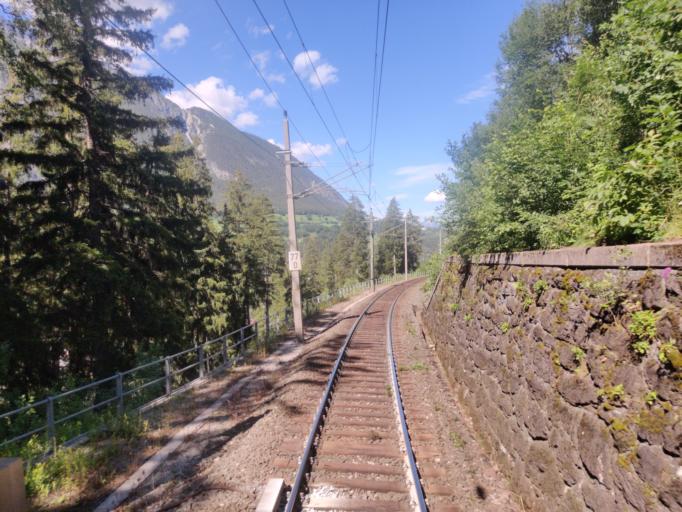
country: AT
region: Tyrol
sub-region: Politischer Bezirk Landeck
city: Pians
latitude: 47.1337
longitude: 10.5210
